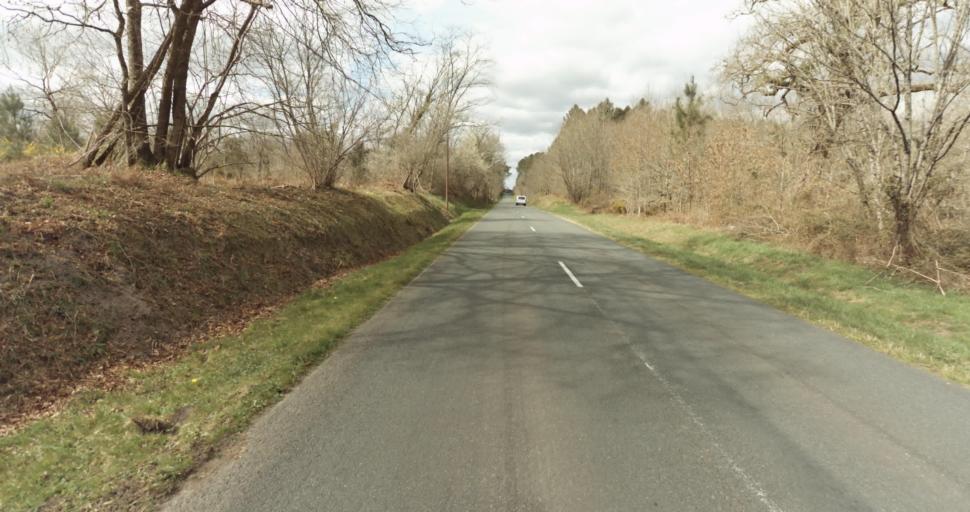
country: FR
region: Aquitaine
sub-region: Departement des Landes
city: Roquefort
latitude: 44.0641
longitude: -0.4101
